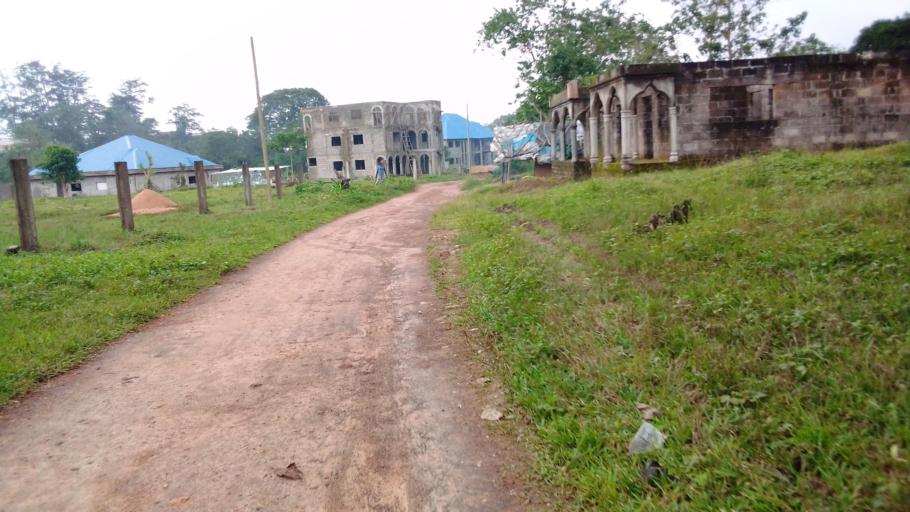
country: SL
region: Eastern Province
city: Kenema
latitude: 7.8871
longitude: -11.1959
